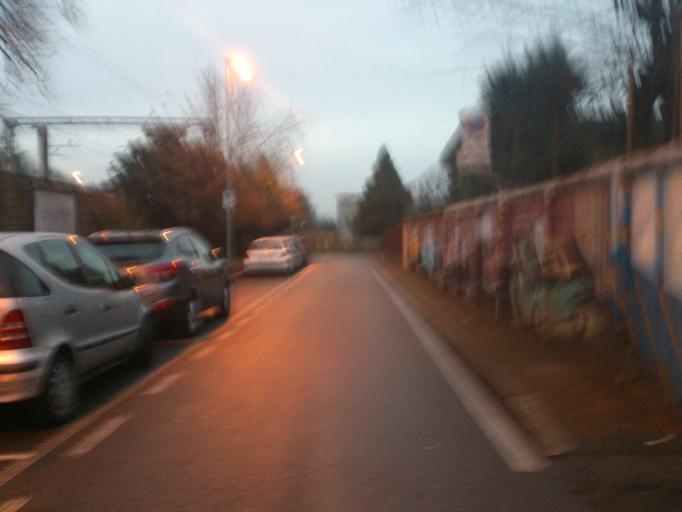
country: IT
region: Lombardy
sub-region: Citta metropolitana di Milano
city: Civesio
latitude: 45.4024
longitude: 9.2733
